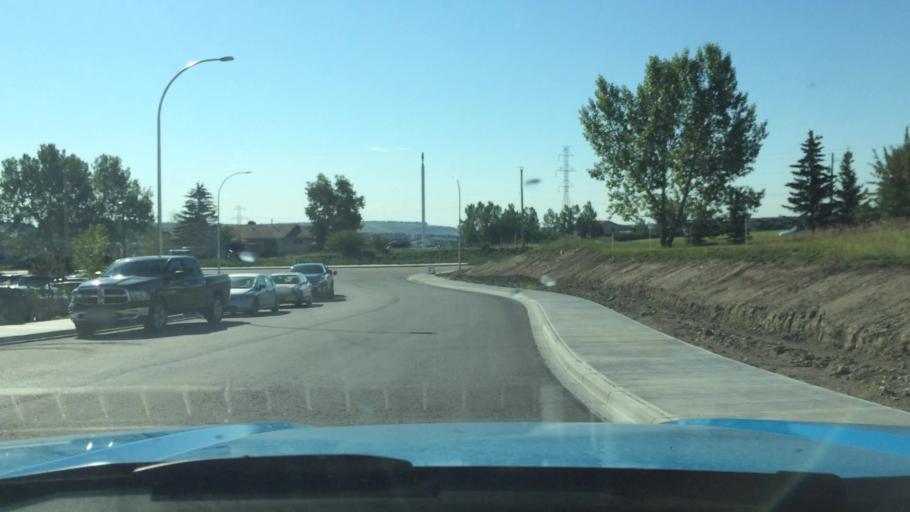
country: CA
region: Alberta
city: Calgary
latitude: 51.1706
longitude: -114.1398
